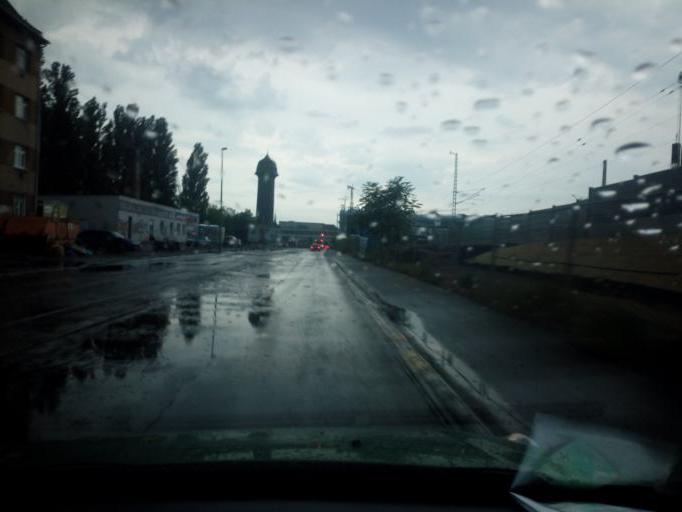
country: DE
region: Berlin
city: Treptow Bezirk
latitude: 52.5024
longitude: 13.4728
